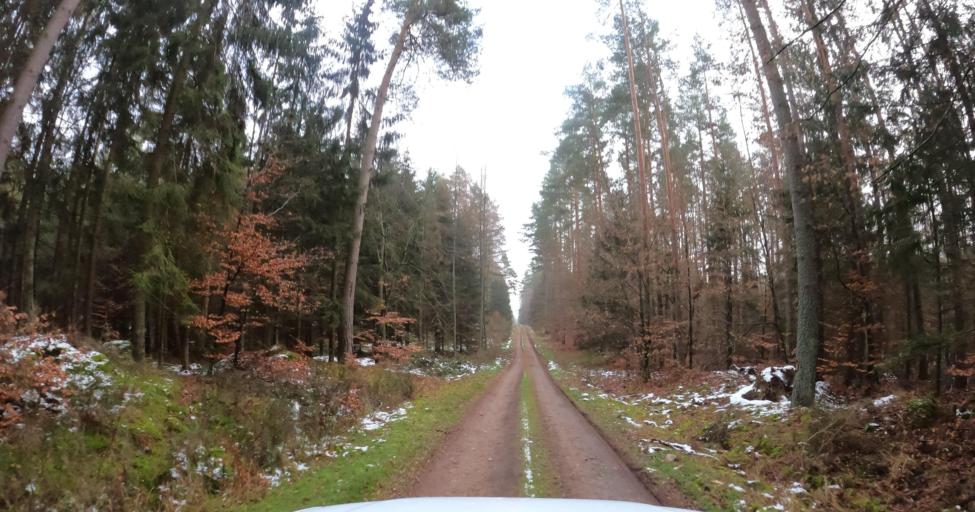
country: PL
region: West Pomeranian Voivodeship
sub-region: Powiat swidwinski
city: Rabino
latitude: 53.9069
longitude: 15.8856
